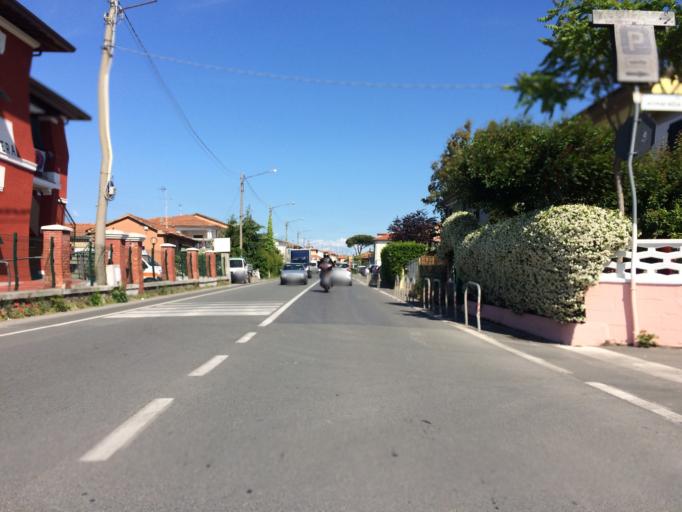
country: IT
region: Liguria
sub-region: Provincia di La Spezia
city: Casano-Dogana-Isola
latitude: 44.0676
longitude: 10.0289
